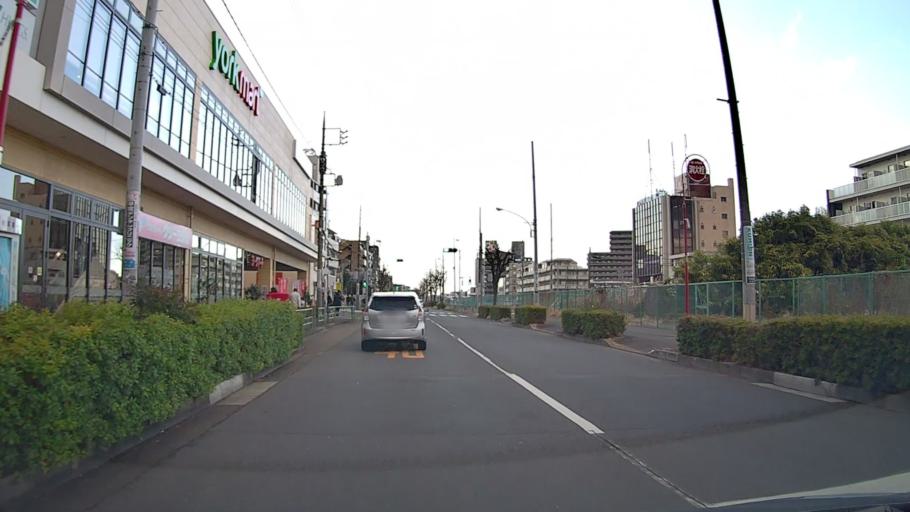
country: JP
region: Saitama
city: Wako
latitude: 35.7560
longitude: 139.6570
